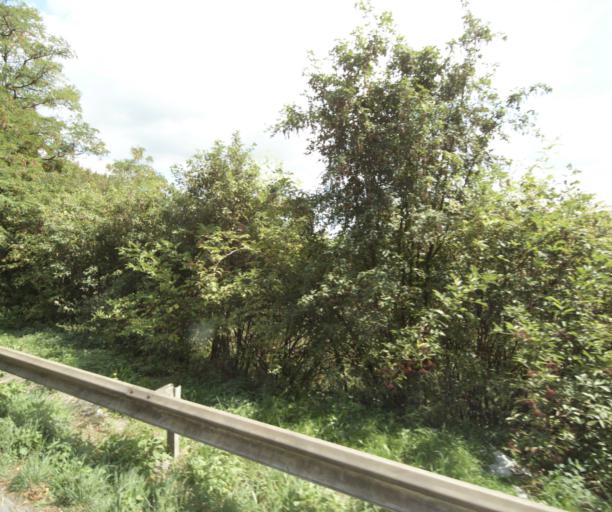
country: FR
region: Nord-Pas-de-Calais
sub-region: Departement du Nord
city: Sainghin-en-Melantois
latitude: 50.5972
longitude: 3.1456
